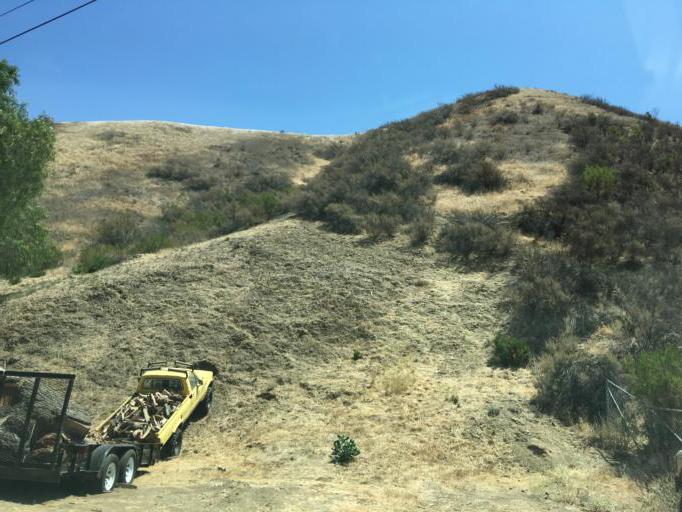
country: US
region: California
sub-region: Los Angeles County
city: Val Verde
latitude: 34.4457
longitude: -118.6731
